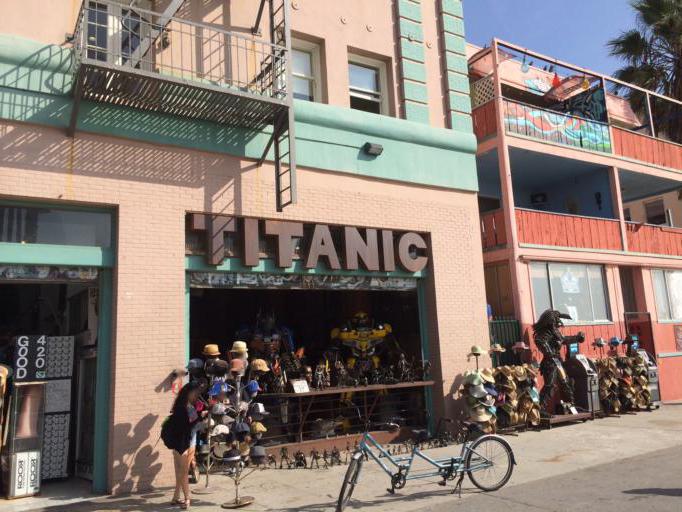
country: US
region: California
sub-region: Los Angeles County
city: Santa Monica
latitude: 33.9939
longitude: -118.4798
